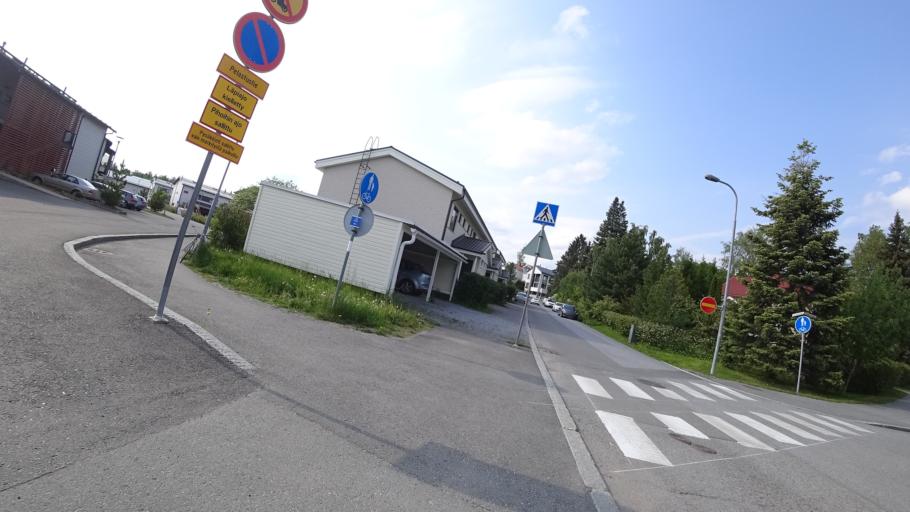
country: FI
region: Pirkanmaa
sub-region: Tampere
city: Pirkkala
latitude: 61.5035
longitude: 23.6882
